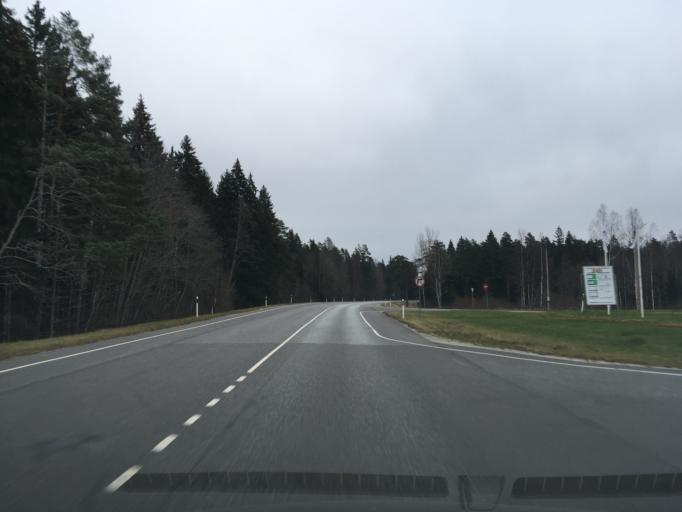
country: EE
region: Laeaene-Virumaa
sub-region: Kadrina vald
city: Kadrina
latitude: 59.4576
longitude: 25.9959
